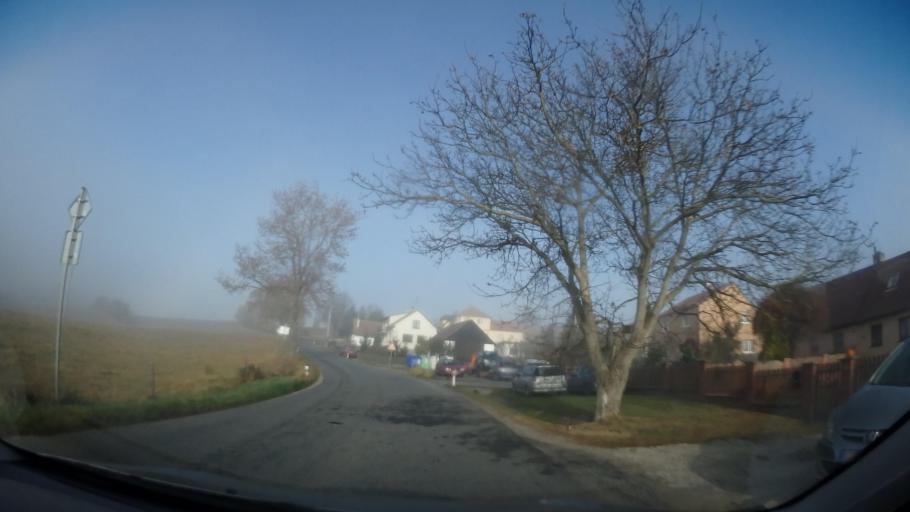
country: CZ
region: Vysocina
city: Bystrice nad Pernstejnem
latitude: 49.4153
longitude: 16.2220
